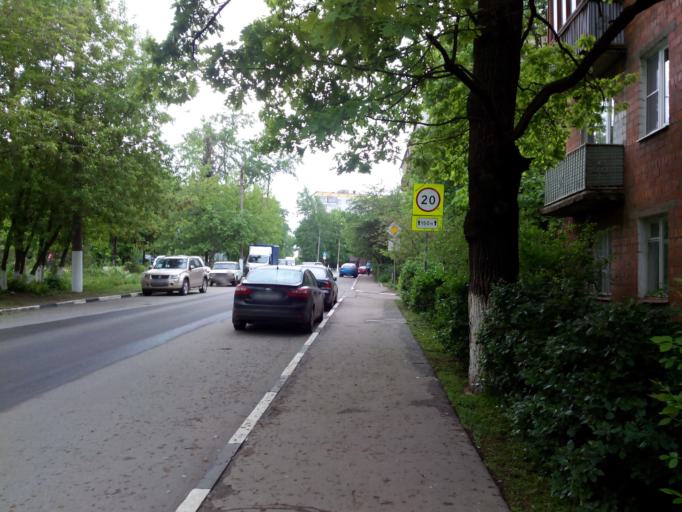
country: RU
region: Moskovskaya
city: Odintsovo
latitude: 55.6644
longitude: 37.2864
